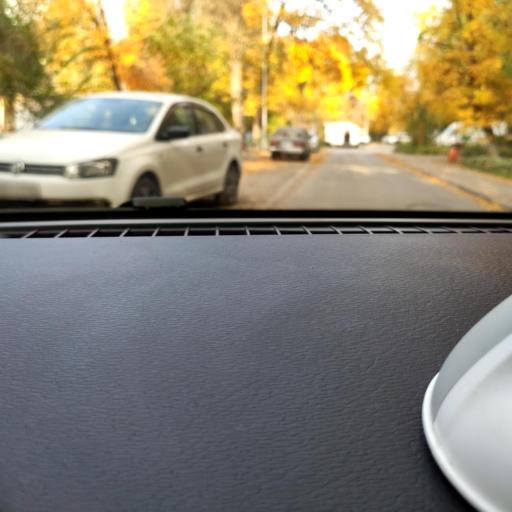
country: RU
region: Samara
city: Samara
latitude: 53.2346
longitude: 50.2169
